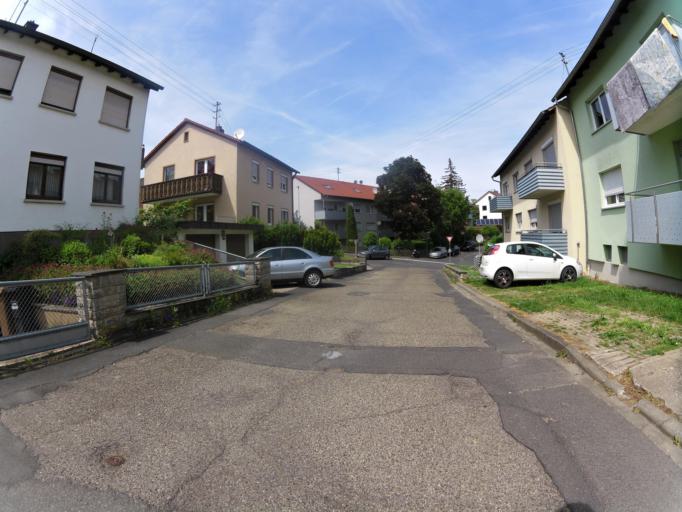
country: DE
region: Bavaria
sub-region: Regierungsbezirk Unterfranken
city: Ochsenfurt
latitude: 49.6679
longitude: 10.0419
